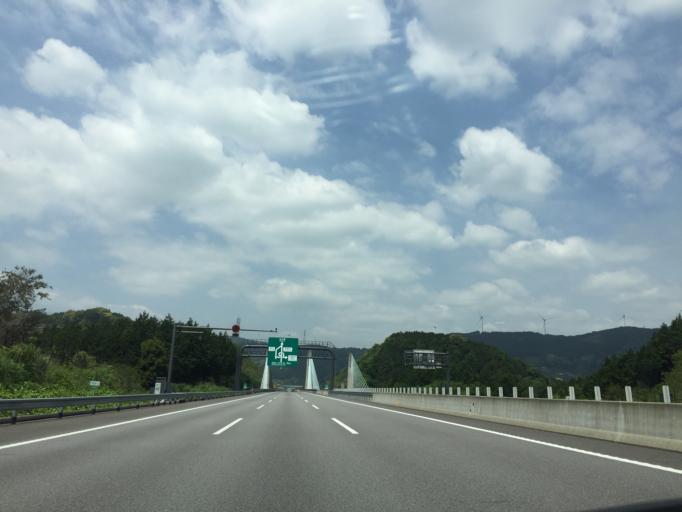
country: JP
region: Shizuoka
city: Hamakita
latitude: 34.8463
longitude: 137.7340
